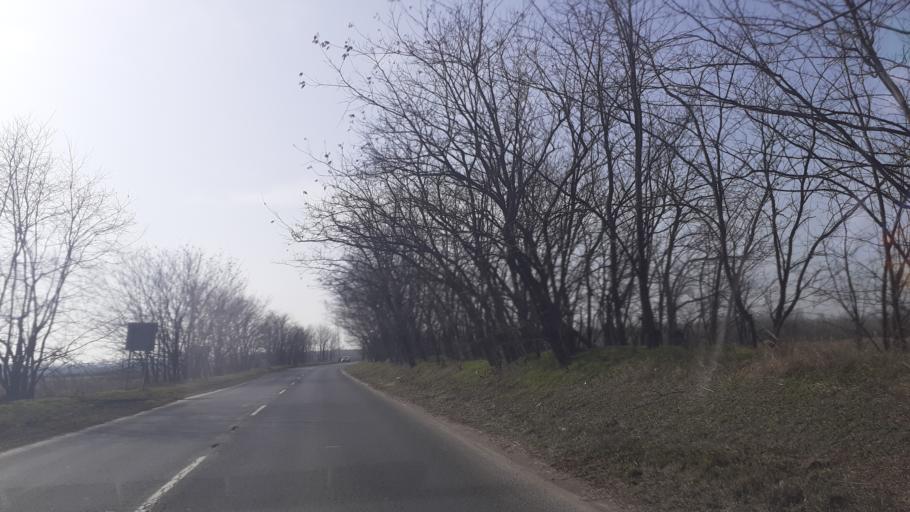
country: HU
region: Pest
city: Orkeny
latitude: 47.1434
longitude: 19.4586
